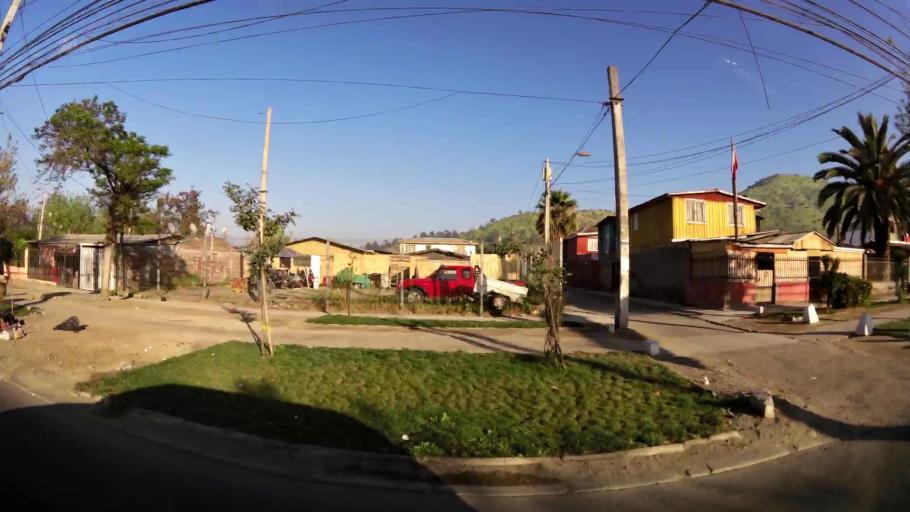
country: CL
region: Santiago Metropolitan
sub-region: Provincia de Santiago
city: Santiago
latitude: -33.3718
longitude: -70.6361
